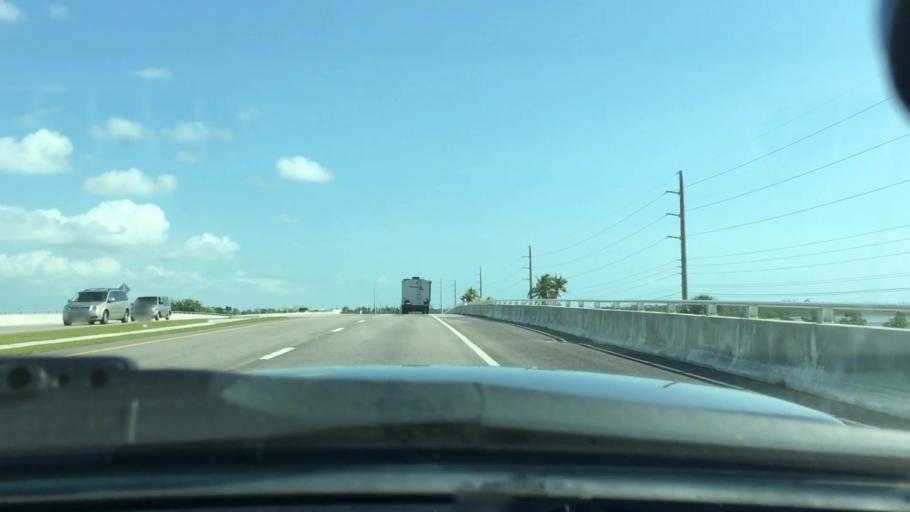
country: US
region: Florida
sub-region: Monroe County
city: Big Coppitt Key
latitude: 24.5879
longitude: -81.6914
